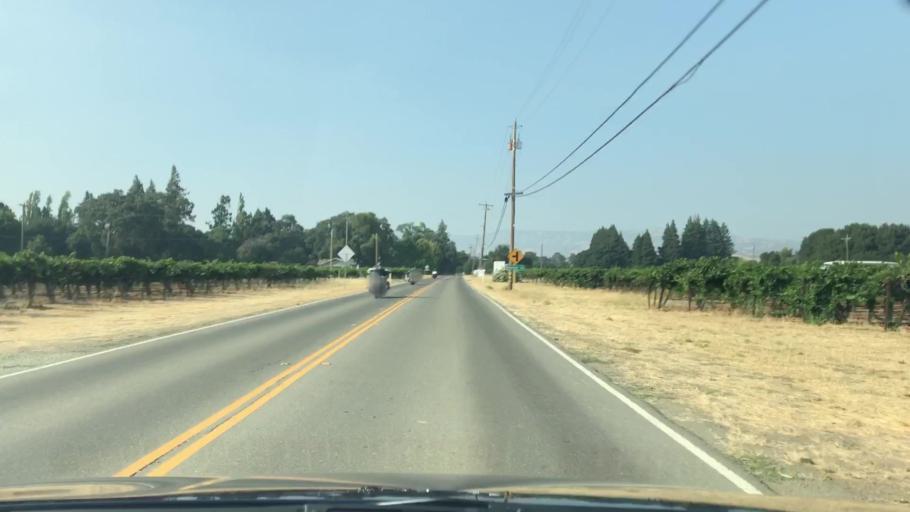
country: US
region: California
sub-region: Solano County
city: Green Valley
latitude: 38.2652
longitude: -122.1133
